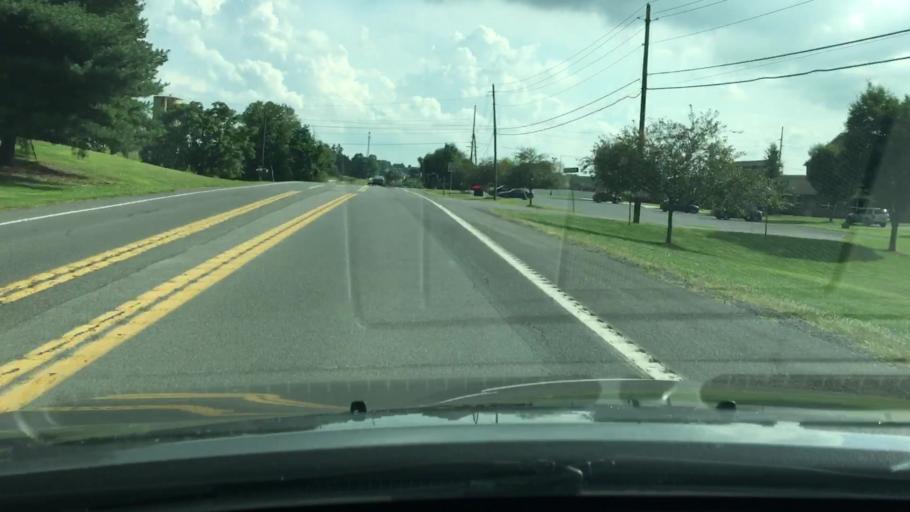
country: US
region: Pennsylvania
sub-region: Franklin County
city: Guilford
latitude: 39.9355
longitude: -77.5906
